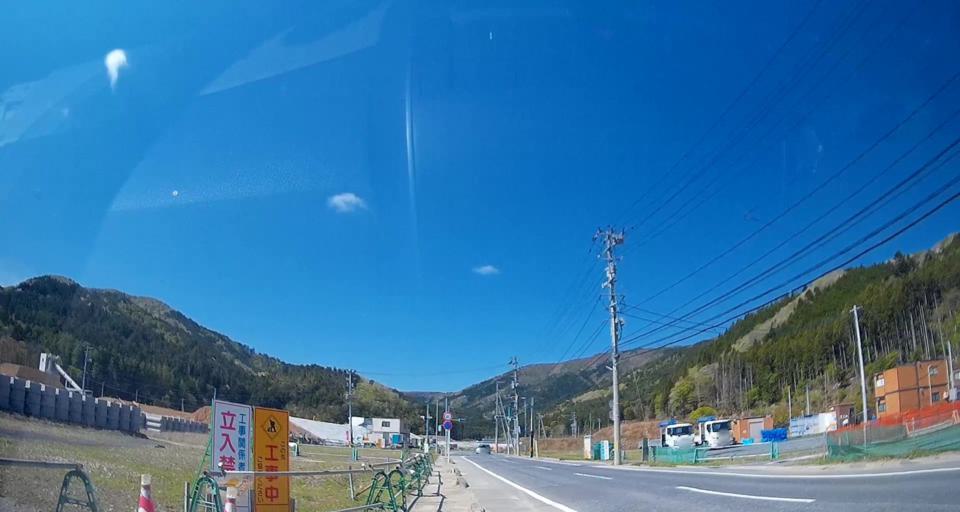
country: JP
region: Miyagi
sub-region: Oshika Gun
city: Onagawa Cho
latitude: 38.5135
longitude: 141.4623
